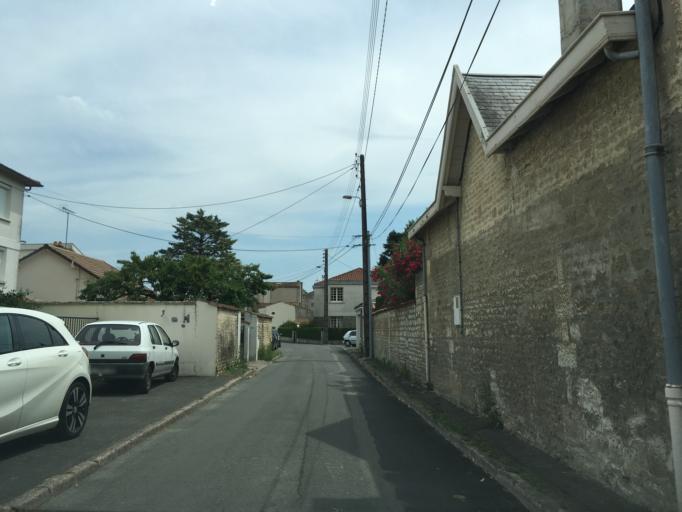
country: FR
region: Poitou-Charentes
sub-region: Departement des Deux-Sevres
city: Niort
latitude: 46.3198
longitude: -0.4708
